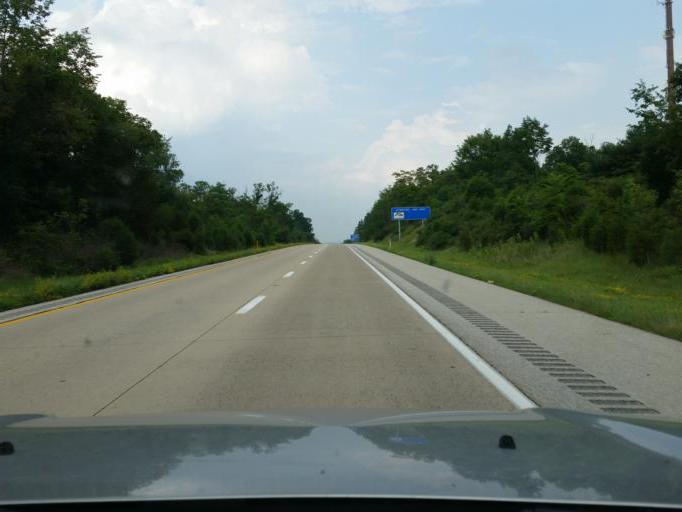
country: US
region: Pennsylvania
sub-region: Adams County
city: Gettysburg
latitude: 39.7665
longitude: -77.2542
